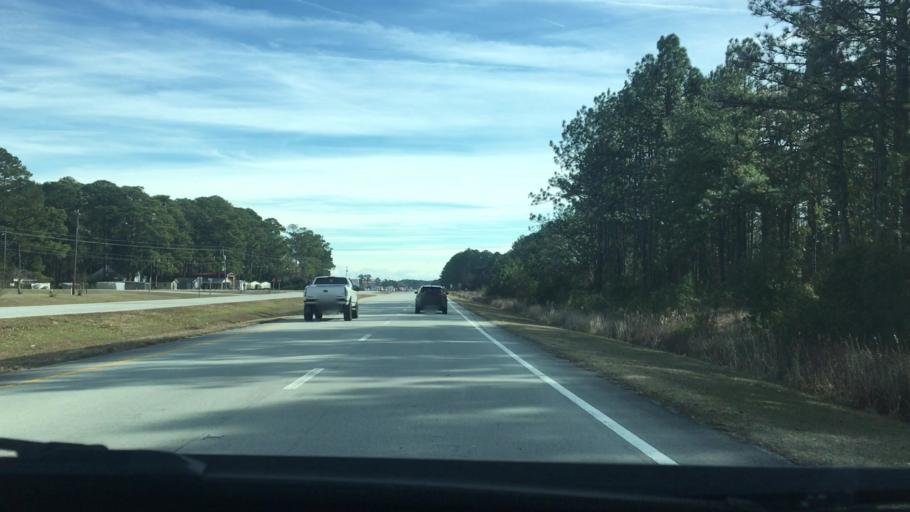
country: US
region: North Carolina
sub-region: Carteret County
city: Newport
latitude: 34.7616
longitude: -76.8542
